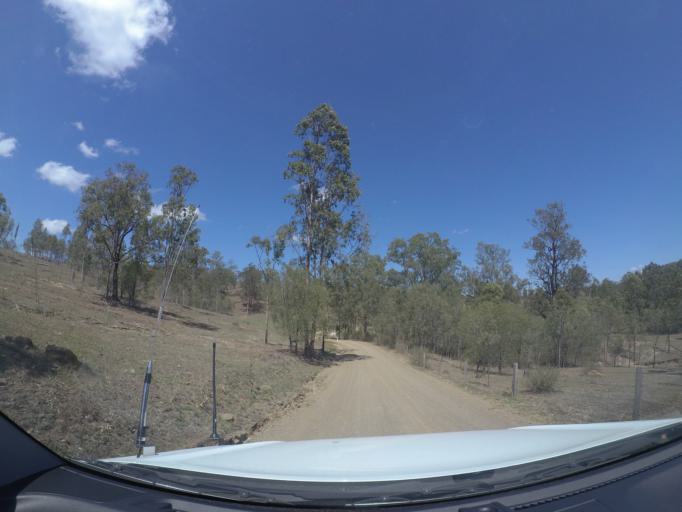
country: AU
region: Queensland
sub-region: Logan
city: Cedar Vale
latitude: -27.8573
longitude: 152.8754
